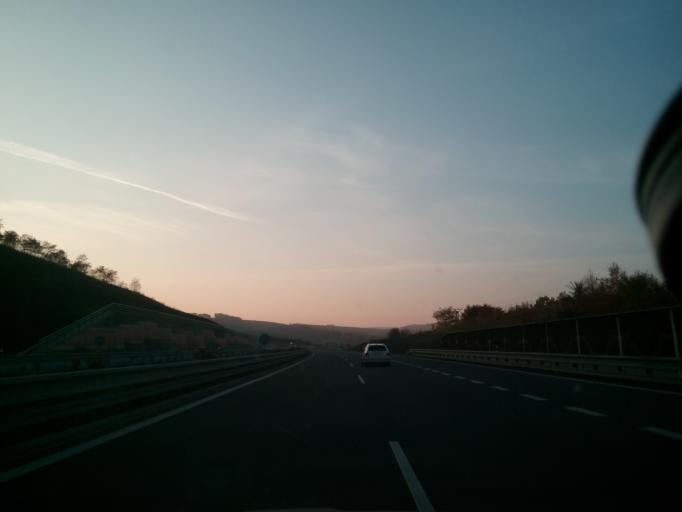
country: SK
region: Presovsky
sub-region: Okres Presov
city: Presov
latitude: 49.0023
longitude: 21.1805
